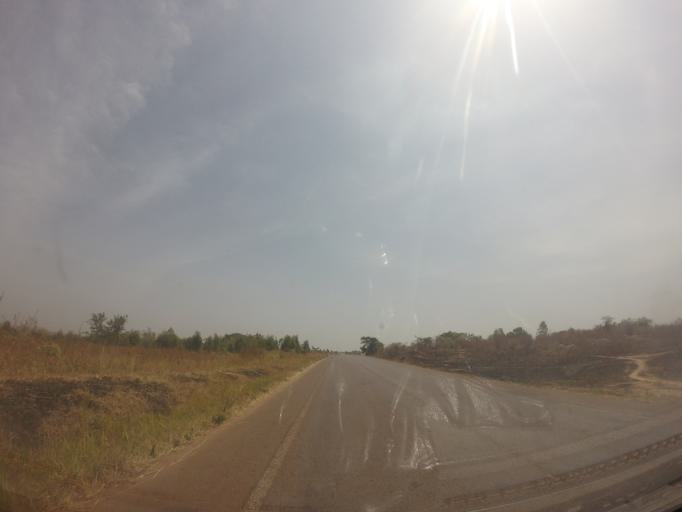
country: UG
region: Northern Region
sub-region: Arua District
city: Arua
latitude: 2.9460
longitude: 30.9472
